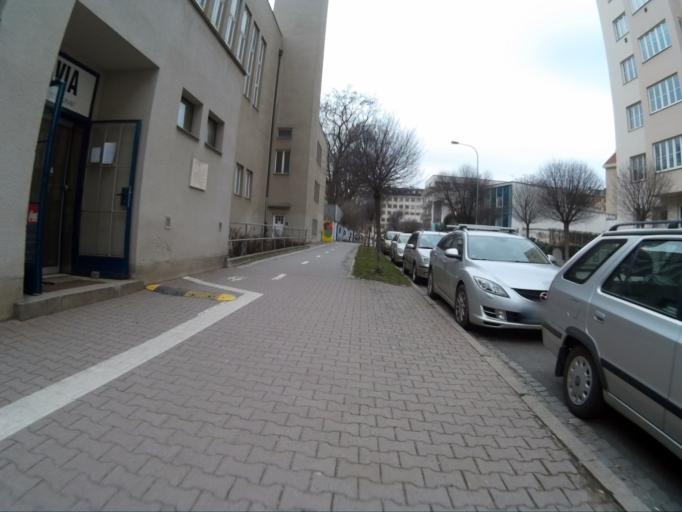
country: CZ
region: South Moravian
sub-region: Mesto Brno
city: Brno
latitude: 49.2035
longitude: 16.6035
